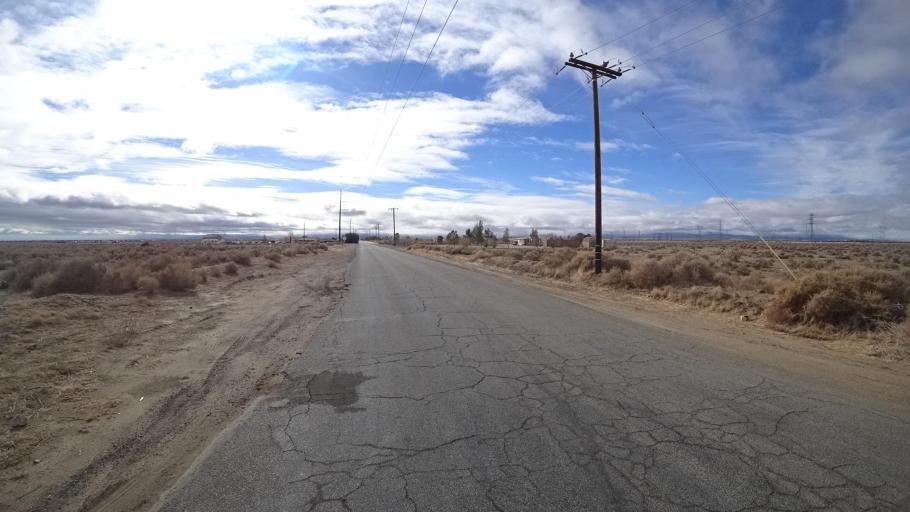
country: US
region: California
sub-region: Kern County
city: Rosamond
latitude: 34.8634
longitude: -118.3090
